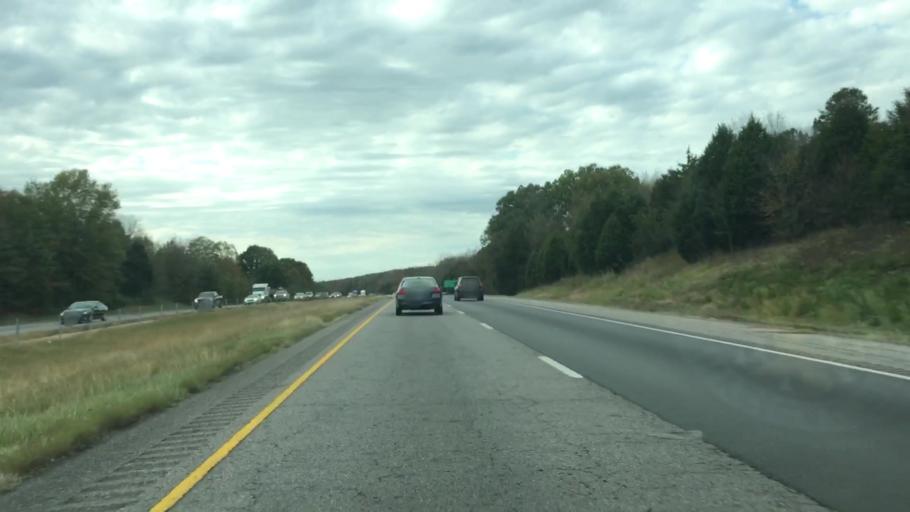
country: US
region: Arkansas
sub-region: Faulkner County
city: Conway
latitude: 35.1560
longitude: -92.5630
